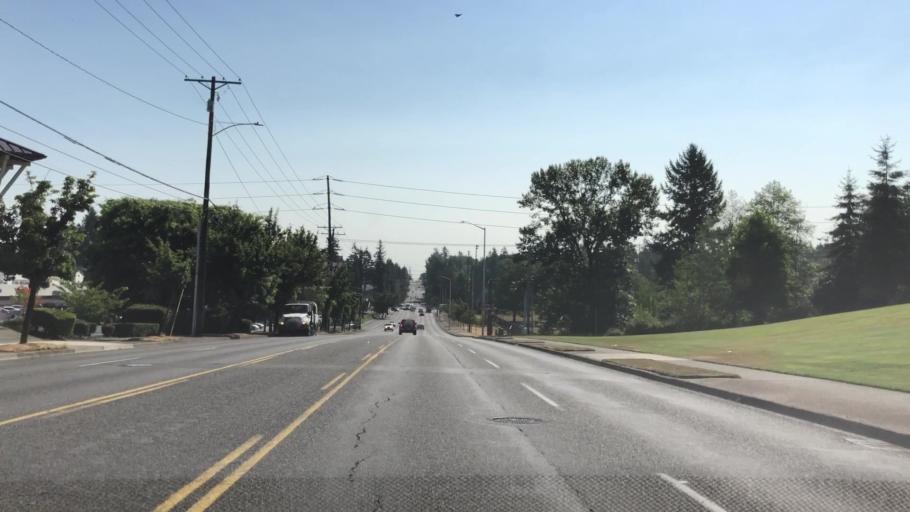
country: US
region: Washington
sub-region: Pierce County
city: Fircrest
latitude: 47.2428
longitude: -122.4998
